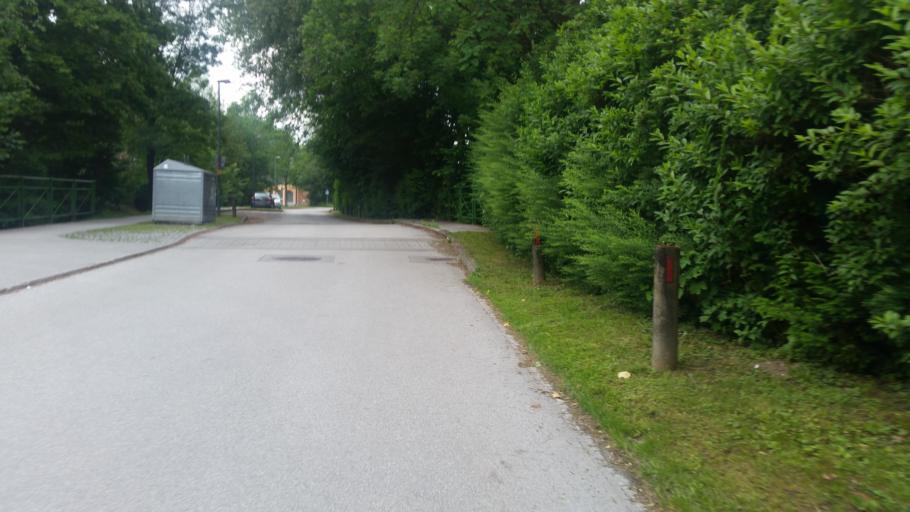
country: AT
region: Salzburg
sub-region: Salzburg Stadt
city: Salzburg
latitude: 47.7950
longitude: 13.0756
